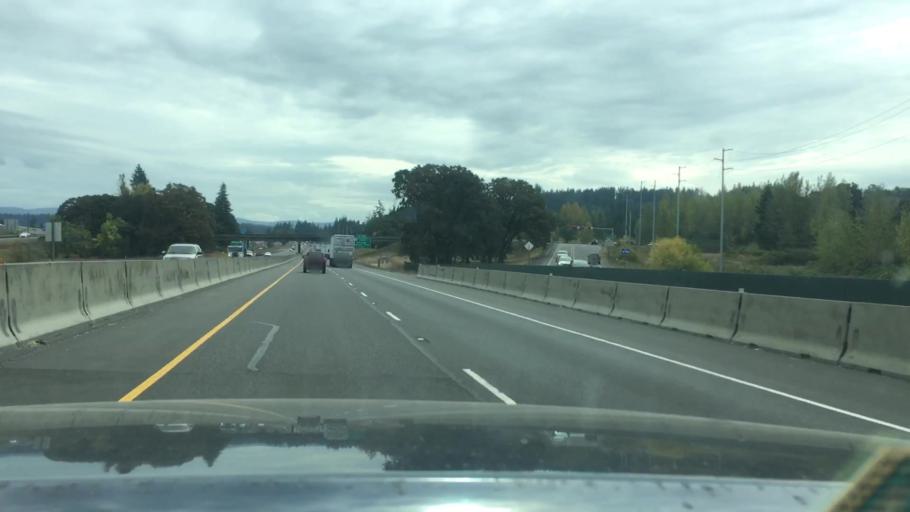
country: US
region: Oregon
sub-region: Lane County
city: Springfield
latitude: 44.0163
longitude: -123.0247
